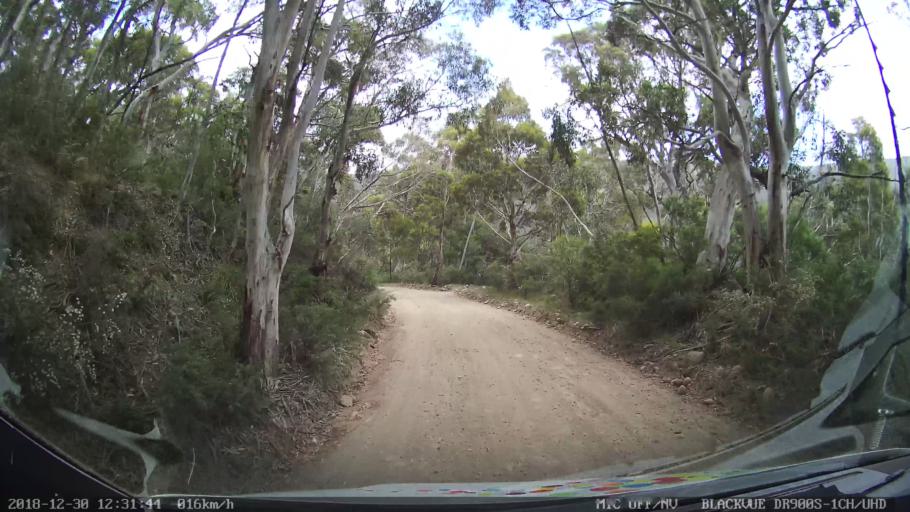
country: AU
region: New South Wales
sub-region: Snowy River
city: Jindabyne
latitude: -36.3239
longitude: 148.4698
